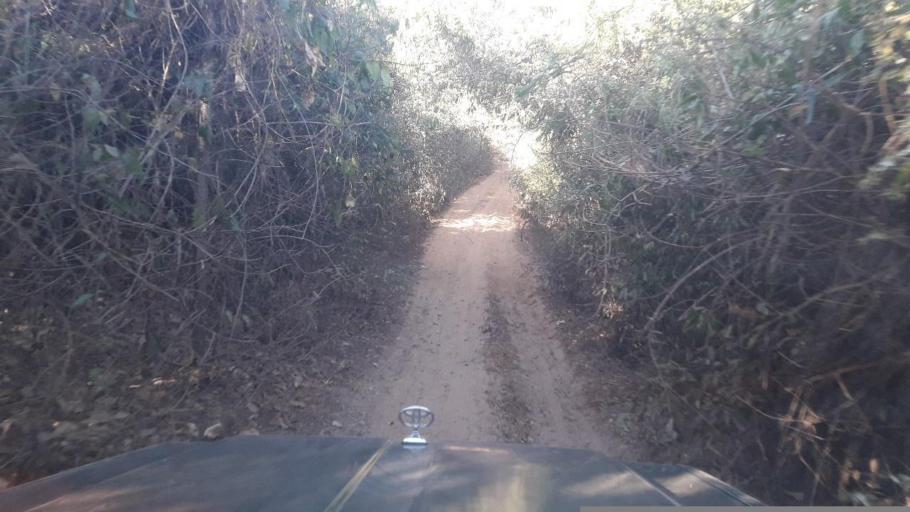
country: MG
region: Boeny
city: Sitampiky
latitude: -16.4272
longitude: 45.6263
